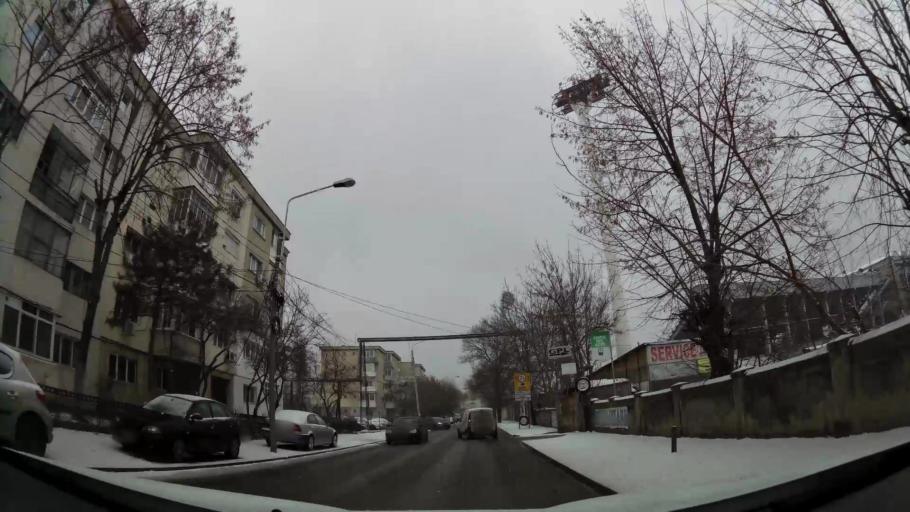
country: RO
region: Prahova
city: Ploiesti
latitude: 44.9275
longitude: 26.0038
